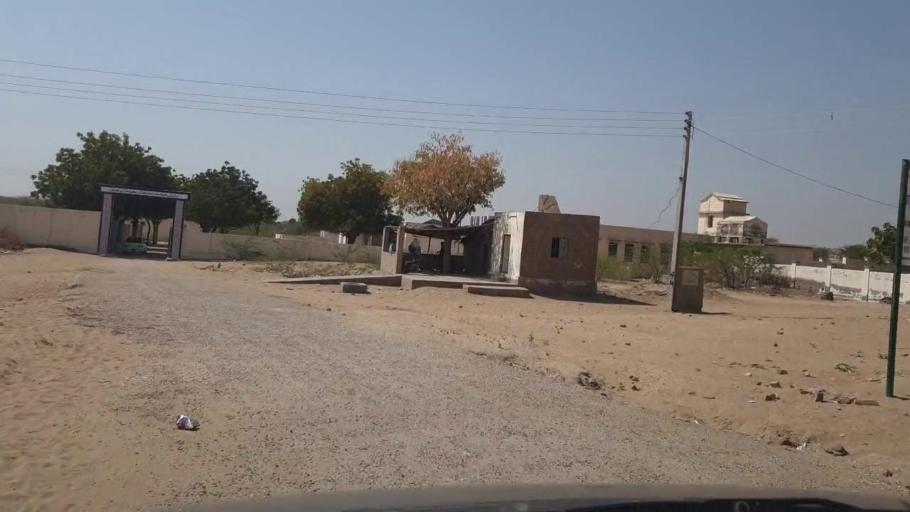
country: PK
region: Sindh
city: Chor
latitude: 25.5691
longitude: 70.1848
